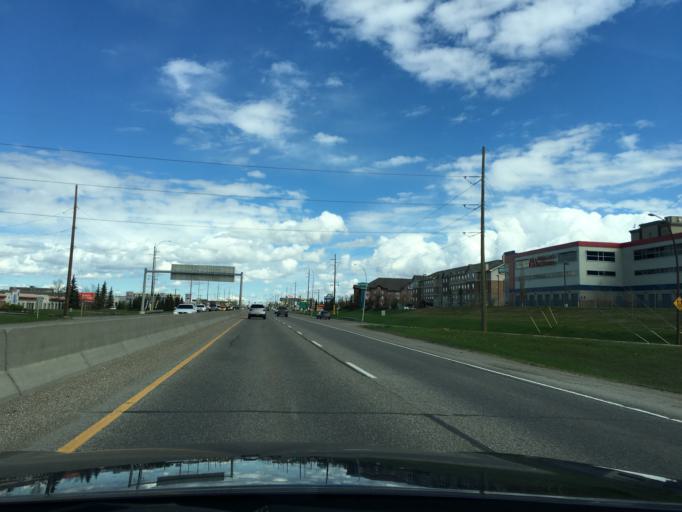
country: CA
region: Alberta
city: Calgary
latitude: 51.0696
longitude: -114.0016
